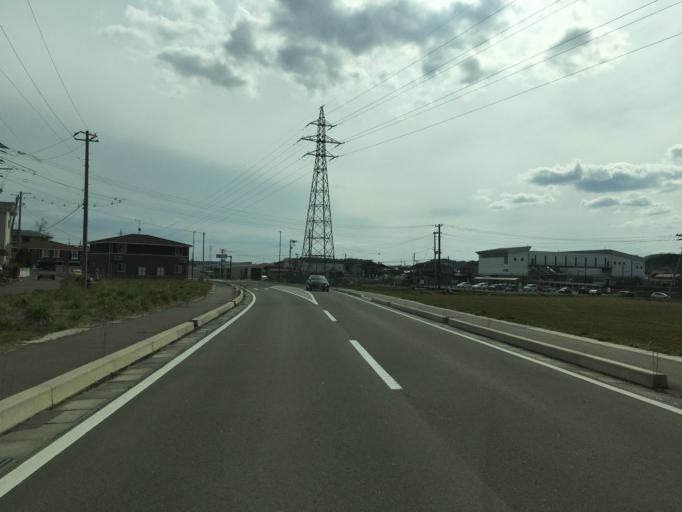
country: JP
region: Fukushima
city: Nihommatsu
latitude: 37.6135
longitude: 140.4685
